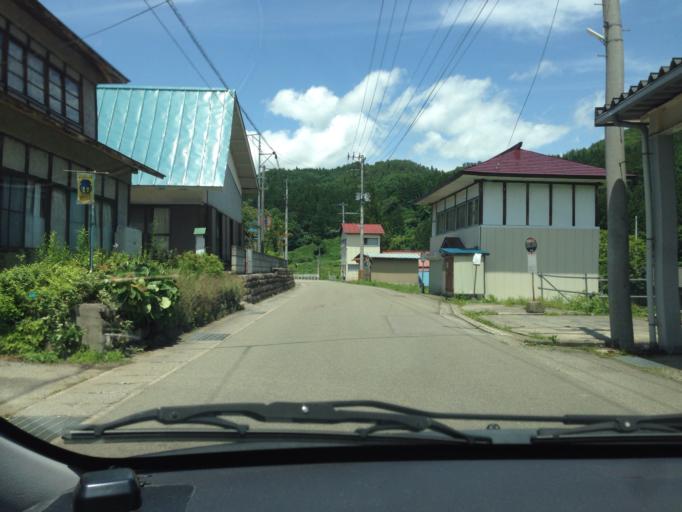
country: JP
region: Tochigi
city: Kuroiso
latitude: 37.2650
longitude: 139.8502
